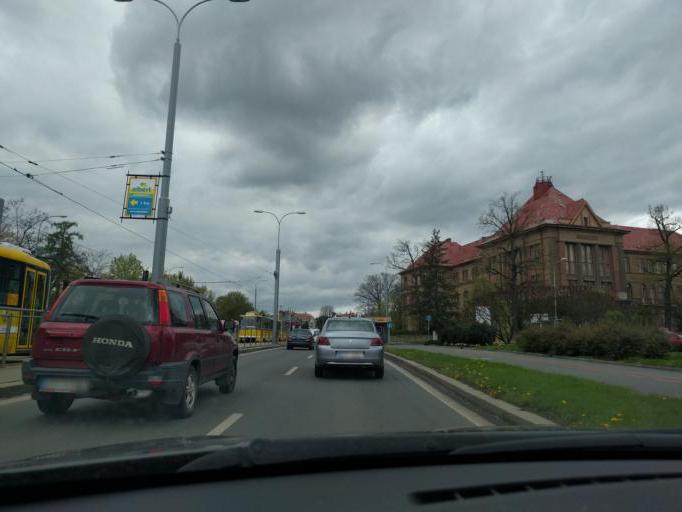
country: CZ
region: Plzensky
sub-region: Okres Plzen-Mesto
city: Pilsen
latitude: 49.7607
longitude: 13.3685
